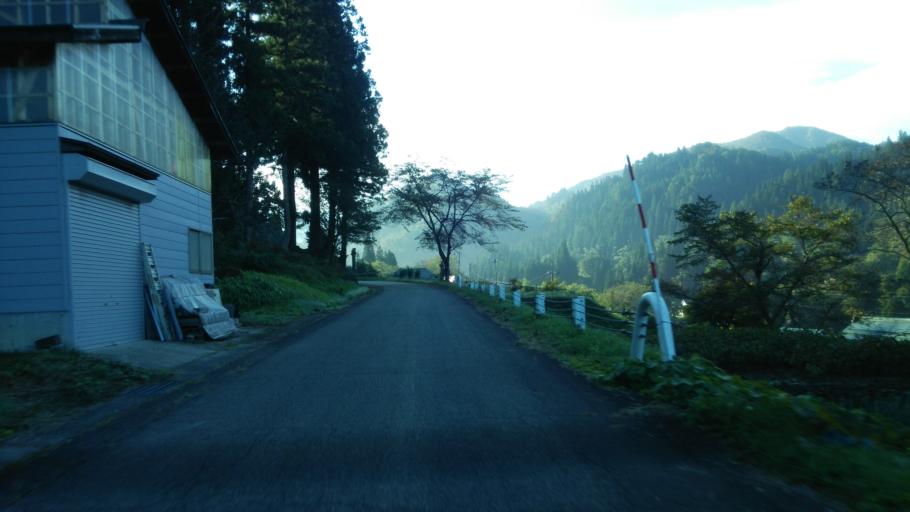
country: JP
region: Fukushima
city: Kitakata
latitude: 37.4425
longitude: 139.7164
